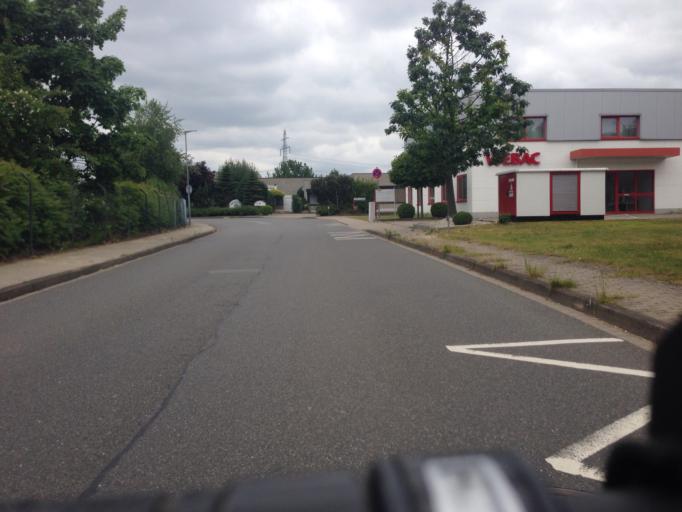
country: DE
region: Schleswig-Holstein
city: Barsbuettel
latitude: 53.5744
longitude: 10.1934
